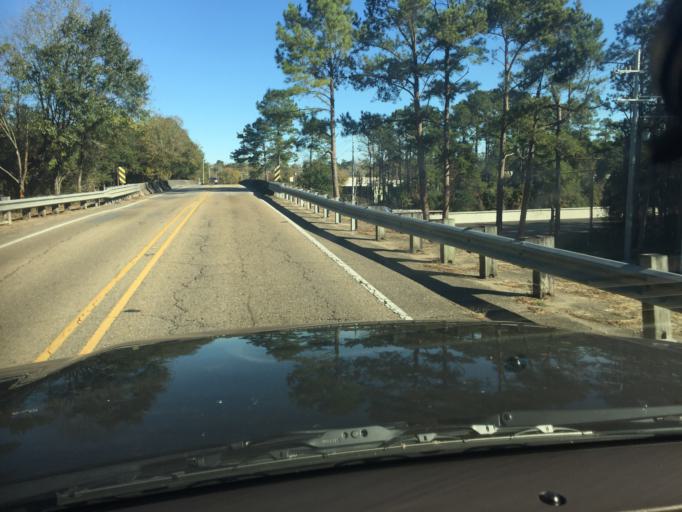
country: US
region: Louisiana
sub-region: Saint Tammany Parish
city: Slidell
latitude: 30.3077
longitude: -89.7491
